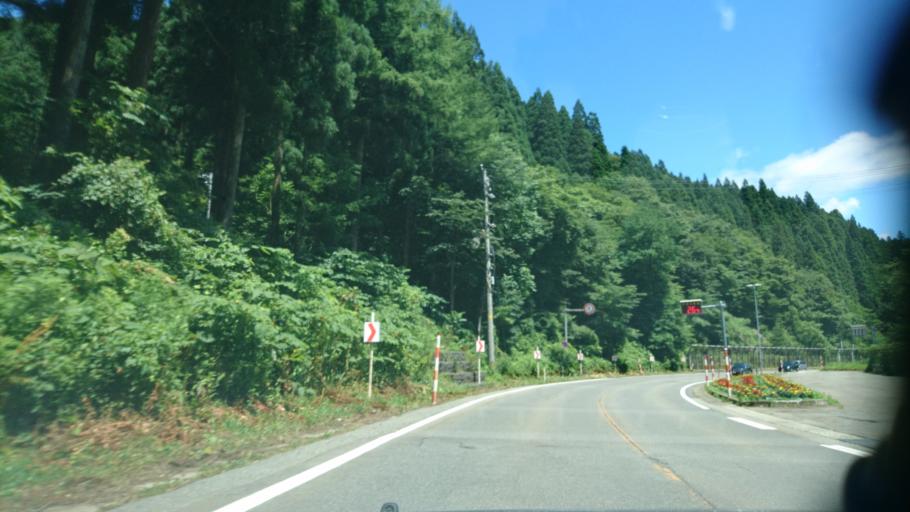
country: JP
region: Akita
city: Kakunodatemachi
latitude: 39.6421
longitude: 140.6605
